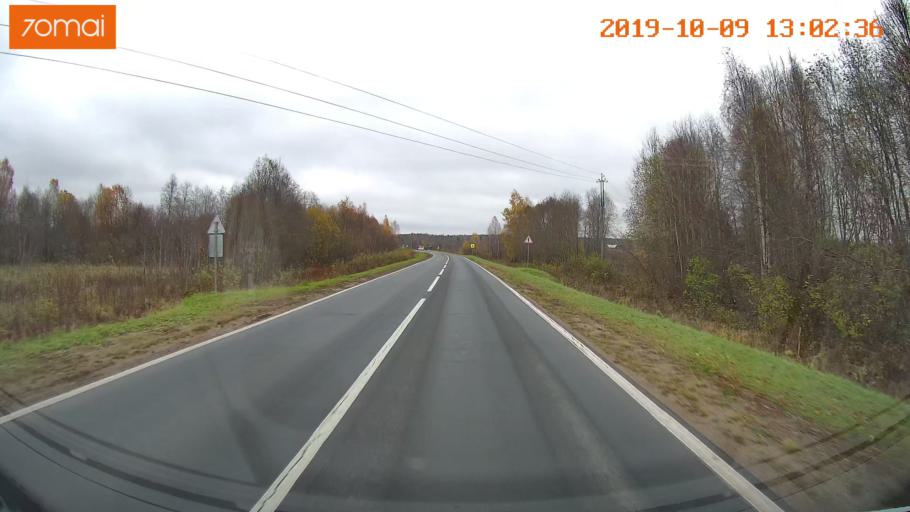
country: RU
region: Jaroslavl
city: Prechistoye
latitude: 58.3605
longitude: 40.5057
